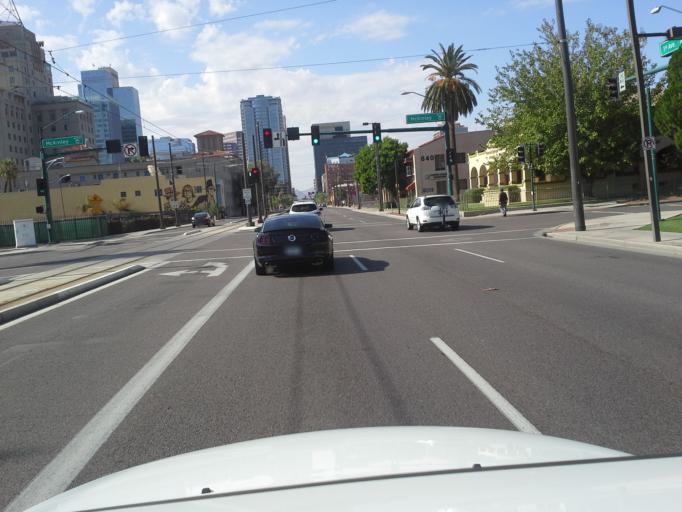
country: US
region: Arizona
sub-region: Maricopa County
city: Phoenix
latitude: 33.4570
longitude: -112.0752
